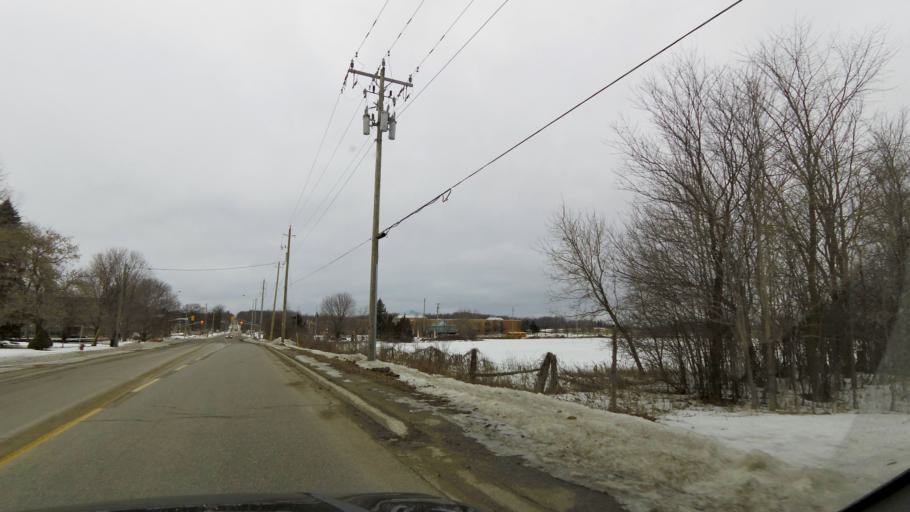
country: CA
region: Ontario
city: Brampton
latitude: 43.8777
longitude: -79.8536
